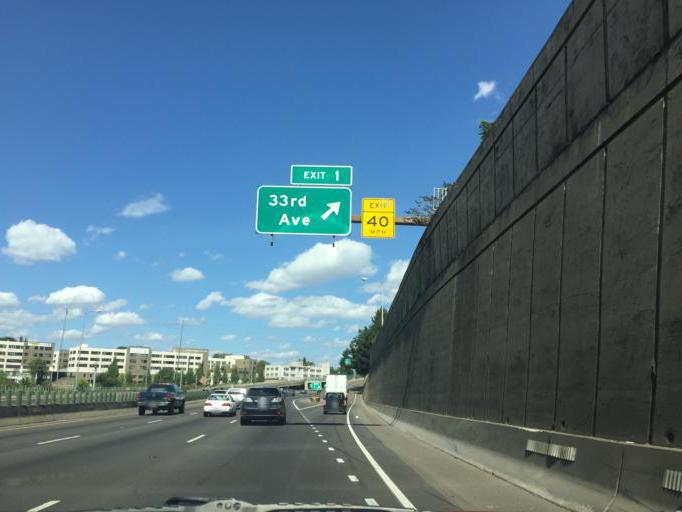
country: US
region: Oregon
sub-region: Multnomah County
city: Portland
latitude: 45.5317
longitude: -122.6332
